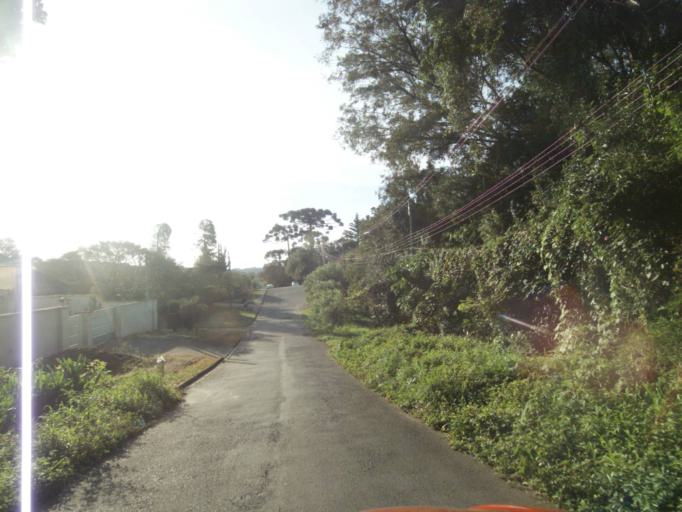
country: BR
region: Parana
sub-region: Curitiba
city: Curitiba
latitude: -25.4296
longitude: -49.3043
